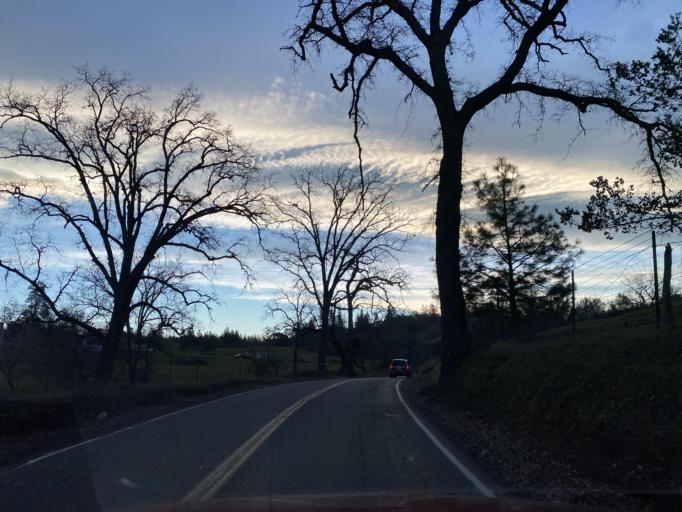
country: US
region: California
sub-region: Amador County
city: Plymouth
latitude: 38.4983
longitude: -120.7362
